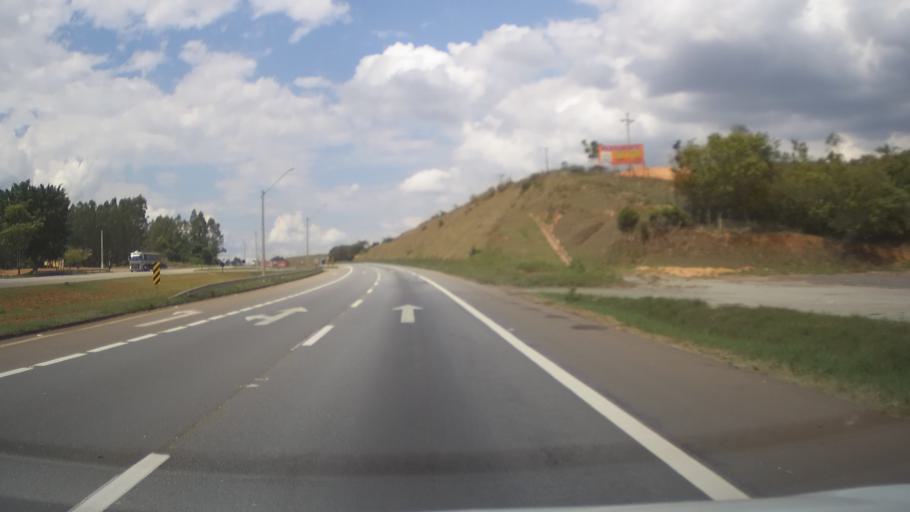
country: BR
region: Minas Gerais
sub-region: Nepomuceno
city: Nepomuceno
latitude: -21.3058
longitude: -45.1575
